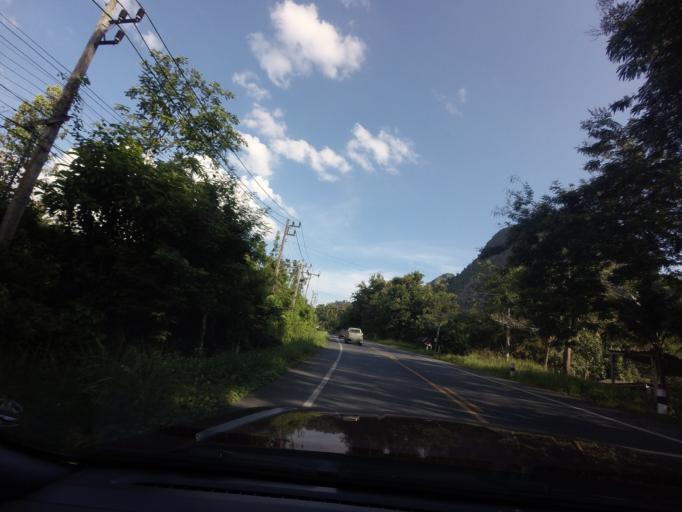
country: TH
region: Yala
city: Than To
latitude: 6.2193
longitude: 101.1650
